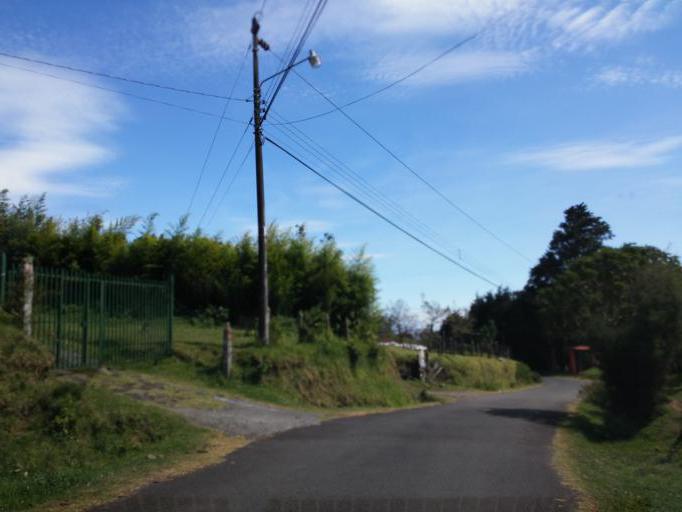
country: CR
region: Heredia
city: Santo Domingo
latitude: 10.1084
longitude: -84.1225
